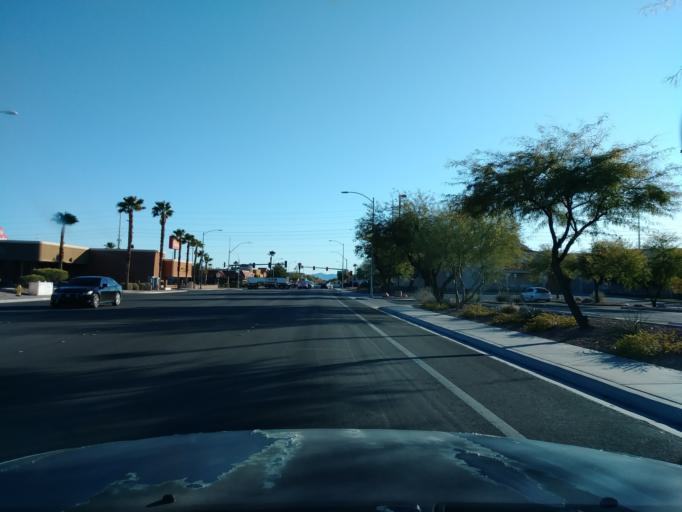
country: US
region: Nevada
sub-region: Clark County
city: Spring Valley
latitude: 36.1453
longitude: -115.2702
